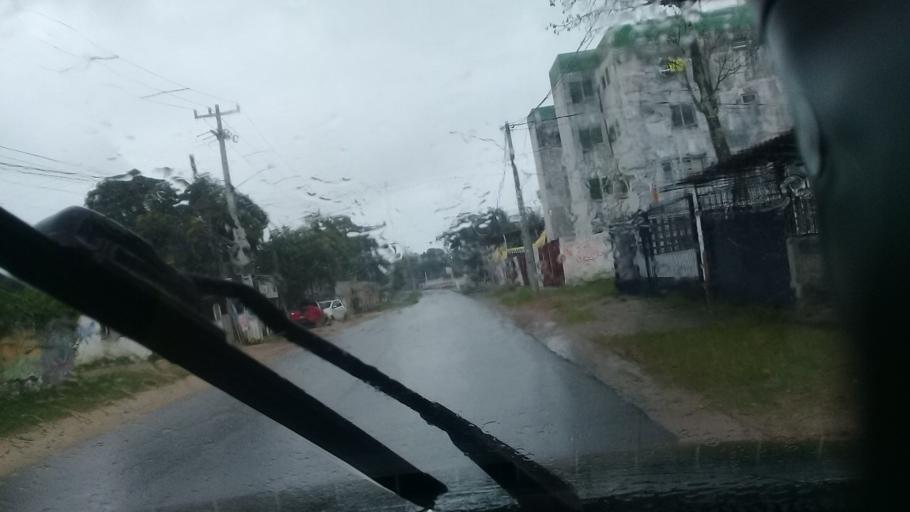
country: BR
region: Pernambuco
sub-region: Itamaraca
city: Itamaraca
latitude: -7.7389
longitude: -34.8249
